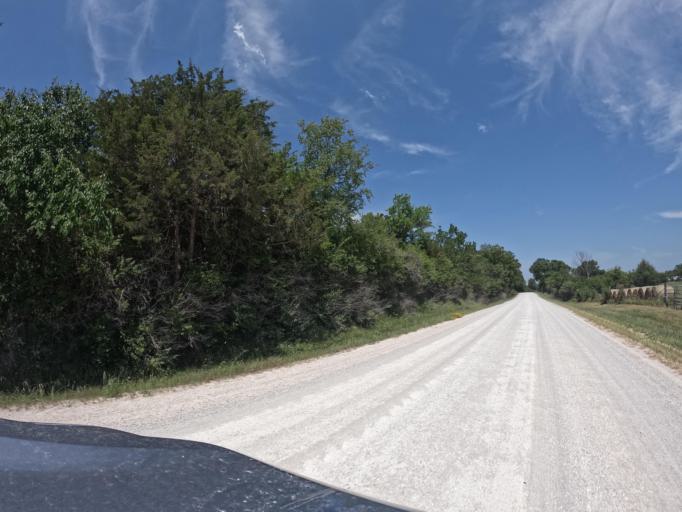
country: US
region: Iowa
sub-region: Henry County
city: Mount Pleasant
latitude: 40.9077
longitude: -91.5469
